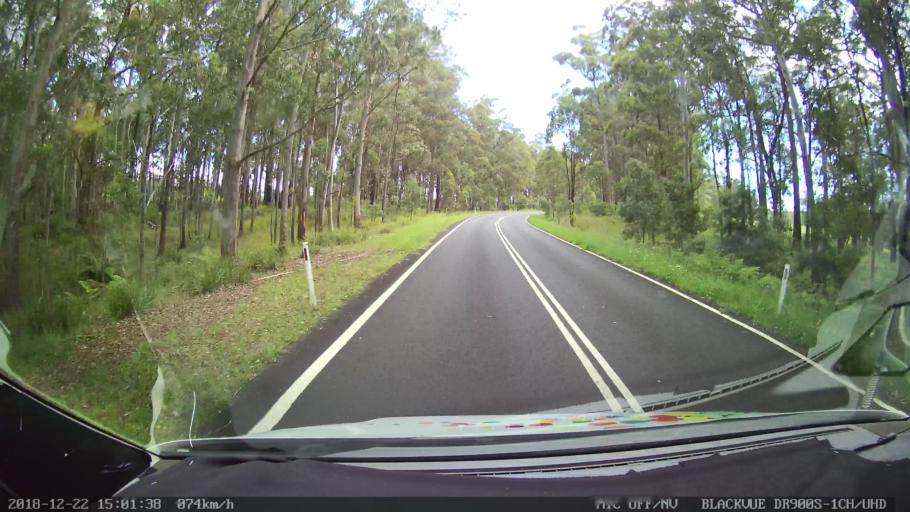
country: AU
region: New South Wales
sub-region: Bellingen
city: Dorrigo
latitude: -30.2565
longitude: 152.4578
